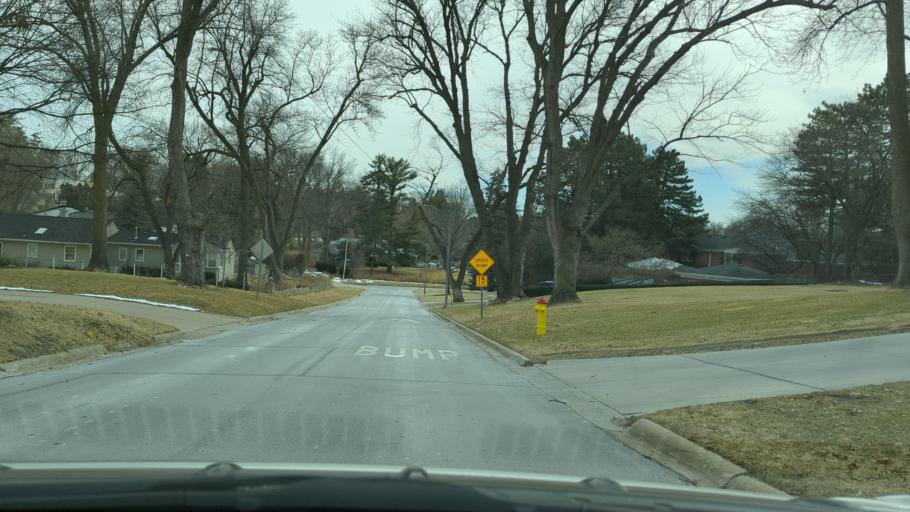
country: US
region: Nebraska
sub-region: Douglas County
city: Ralston
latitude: 41.2660
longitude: -96.0144
